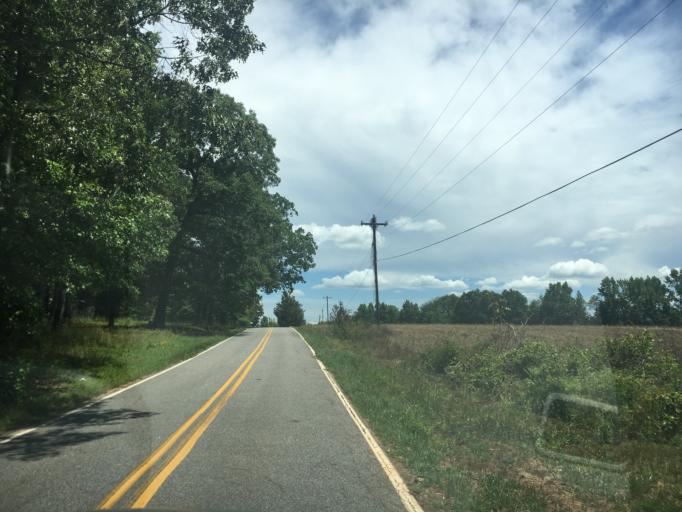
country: US
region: South Carolina
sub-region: Greenville County
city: Five Forks
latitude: 34.8485
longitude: -82.1523
